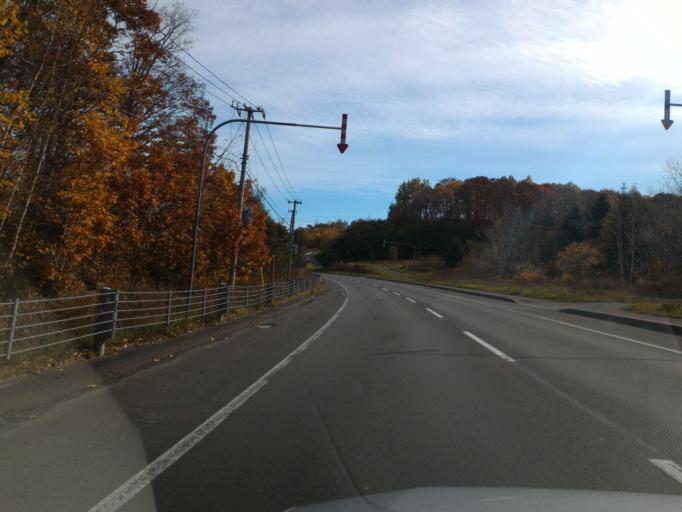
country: JP
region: Hokkaido
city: Shimo-furano
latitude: 43.3684
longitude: 142.3488
